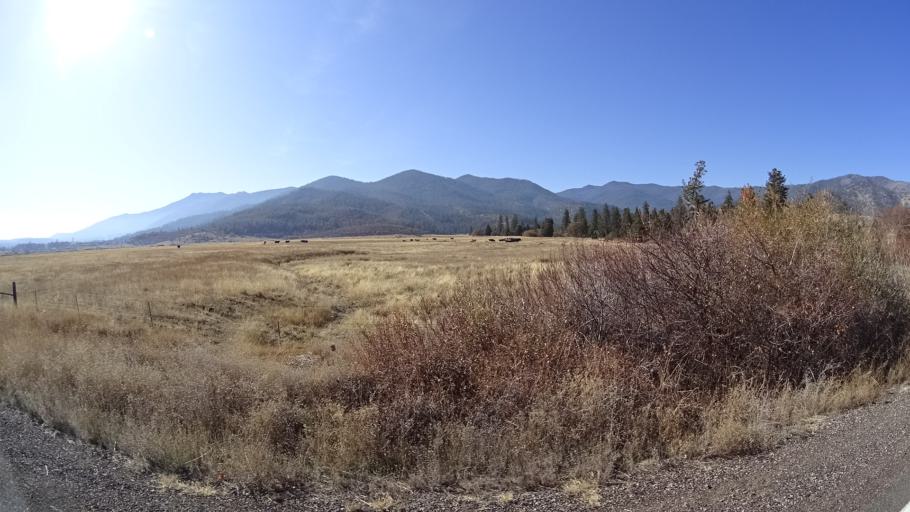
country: US
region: California
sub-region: Siskiyou County
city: Weed
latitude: 41.4477
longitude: -122.4482
